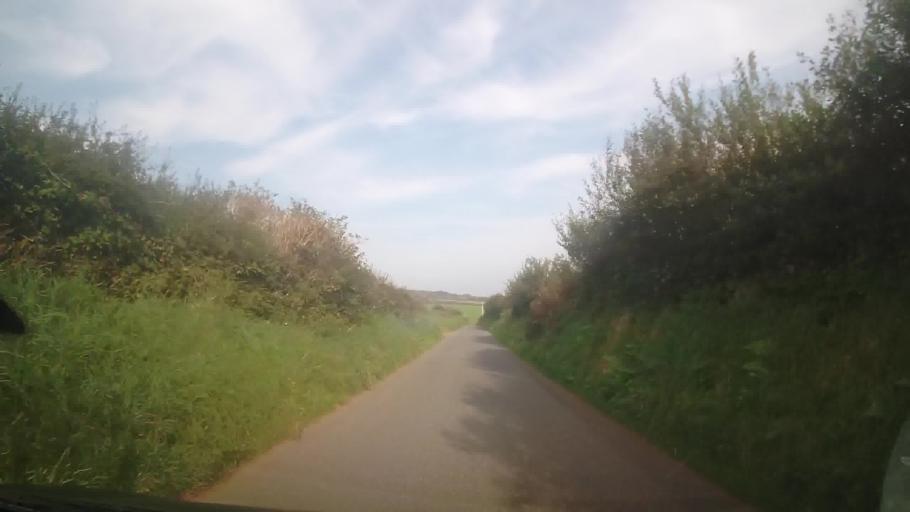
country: GB
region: Wales
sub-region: Pembrokeshire
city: Camrose
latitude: 51.8496
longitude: -5.0737
